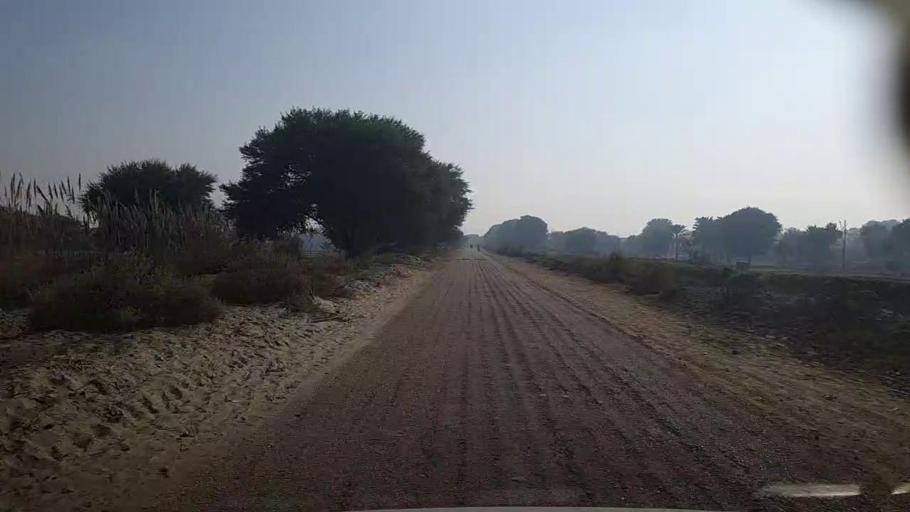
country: PK
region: Sindh
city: Kandiari
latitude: 26.8429
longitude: 68.4894
